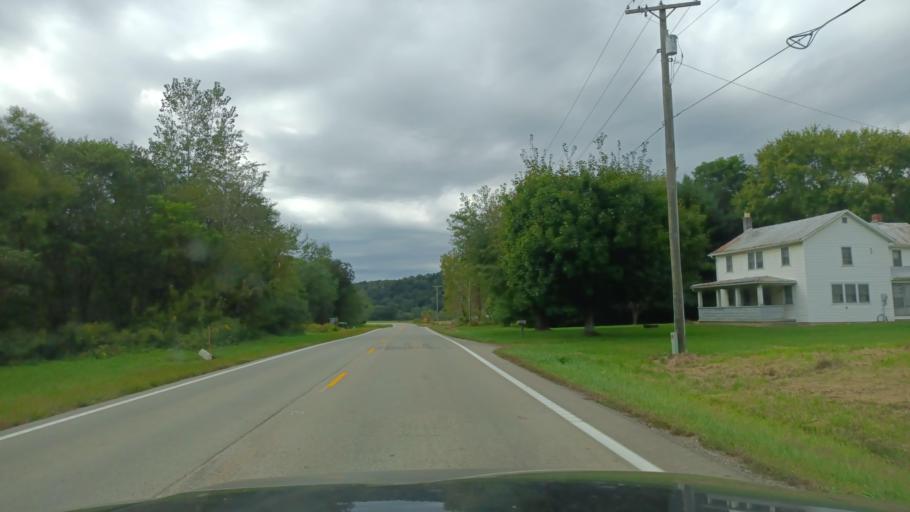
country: US
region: Ohio
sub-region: Vinton County
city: McArthur
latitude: 39.2743
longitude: -82.6166
